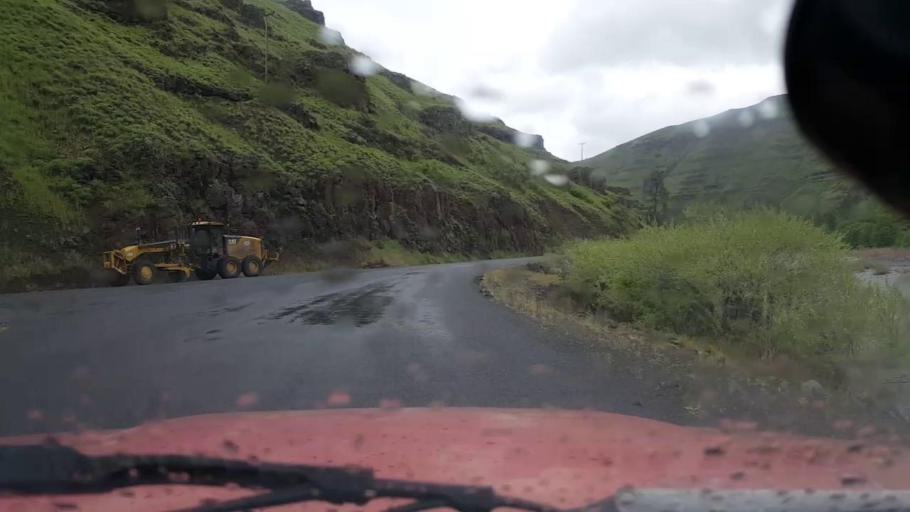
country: US
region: Washington
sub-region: Asotin County
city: Asotin
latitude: 46.0297
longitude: -117.3060
